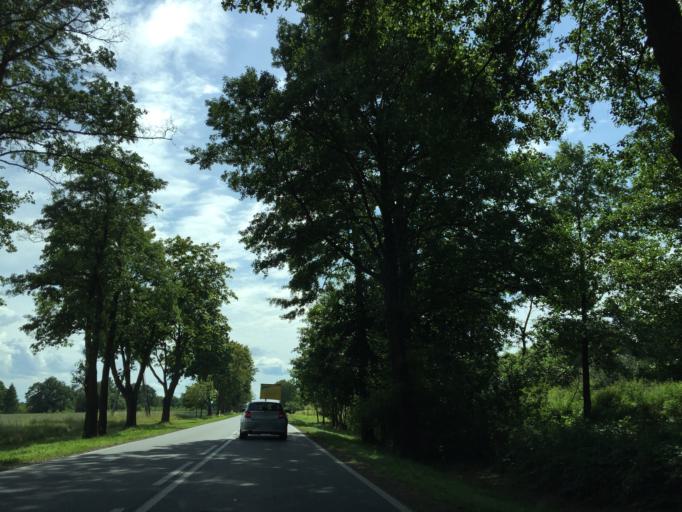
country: PL
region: Masovian Voivodeship
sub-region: Powiat losicki
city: Sarnaki
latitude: 52.3048
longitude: 22.8332
